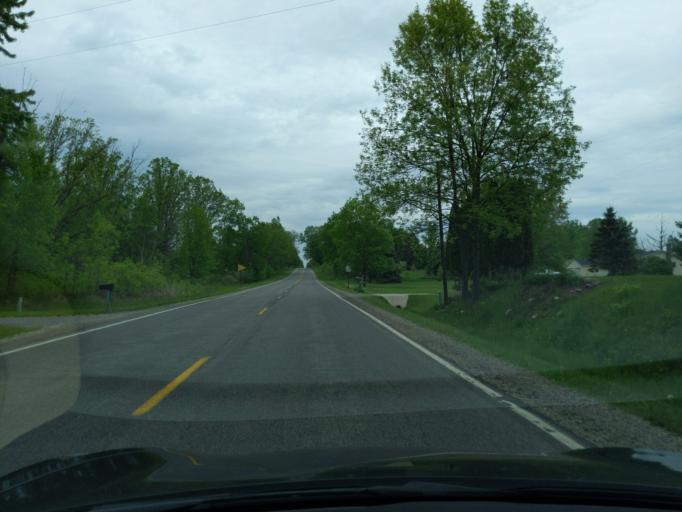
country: US
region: Michigan
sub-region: Ingham County
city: Mason
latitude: 42.5260
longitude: -84.3563
